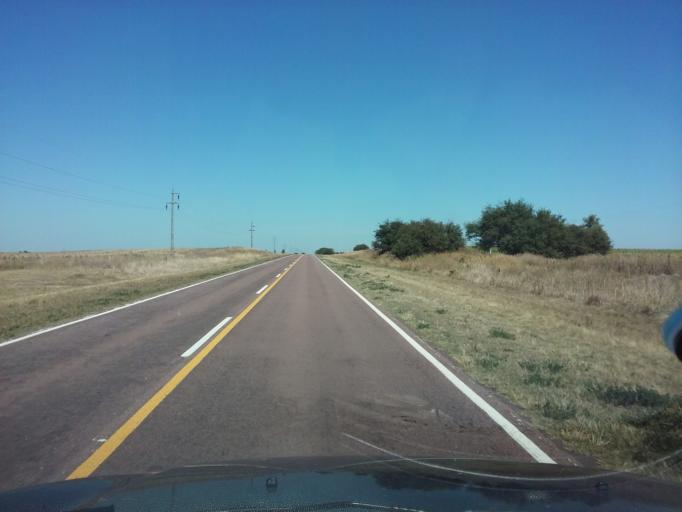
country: AR
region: La Pampa
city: Anguil
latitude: -36.4809
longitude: -63.9436
